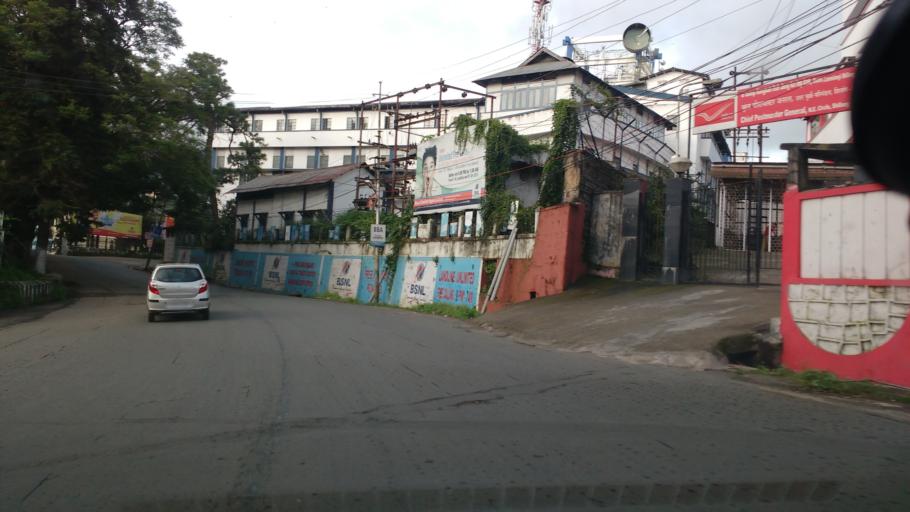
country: IN
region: Meghalaya
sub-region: East Khasi Hills
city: Shillong
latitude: 25.5719
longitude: 91.8870
